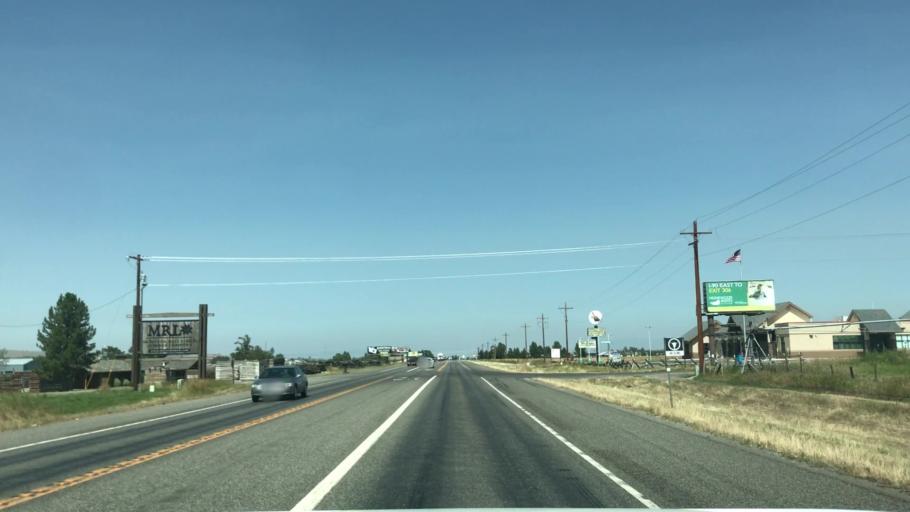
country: US
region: Montana
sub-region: Gallatin County
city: Four Corners
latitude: 45.5830
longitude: -111.1970
